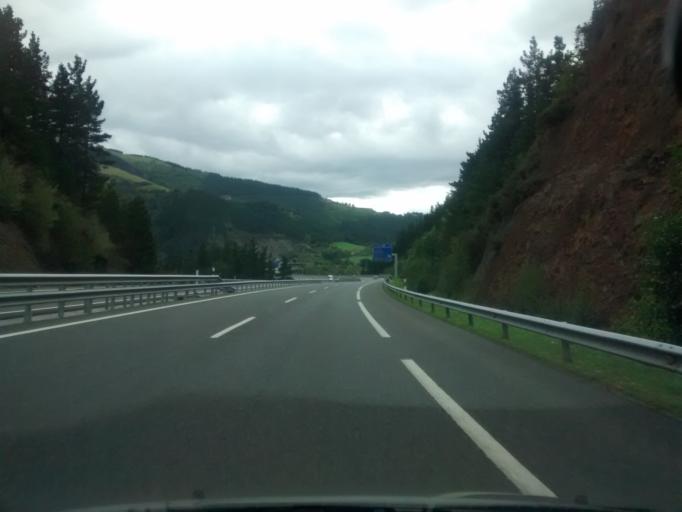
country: ES
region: Basque Country
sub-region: Provincia de Guipuzcoa
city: Bergara
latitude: 43.0968
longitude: -2.4339
